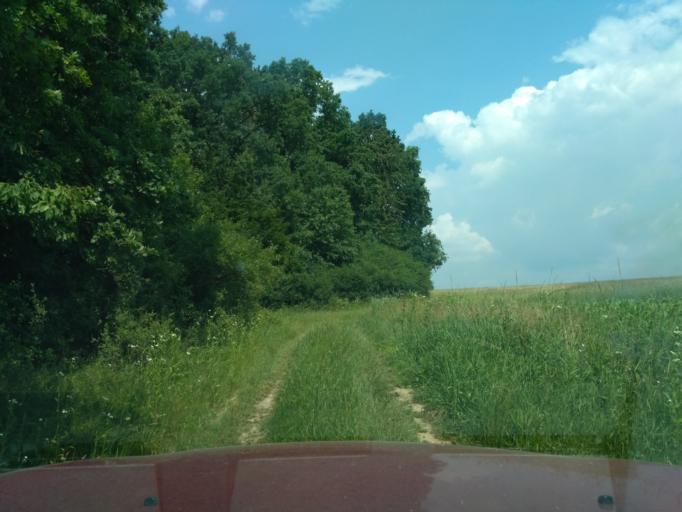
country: SK
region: Kosicky
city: Moldava nad Bodvou
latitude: 48.6230
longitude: 21.0469
